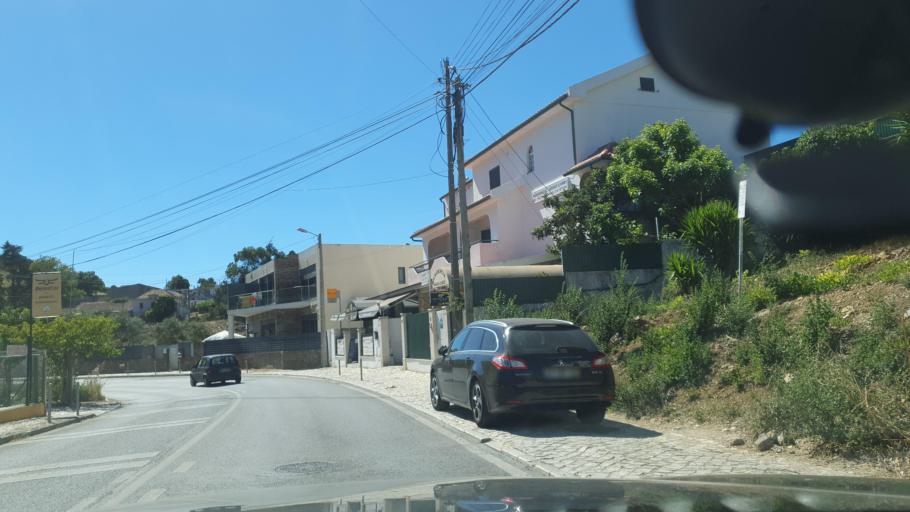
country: PT
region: Lisbon
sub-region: Sintra
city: Belas
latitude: 38.7816
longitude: -9.2507
